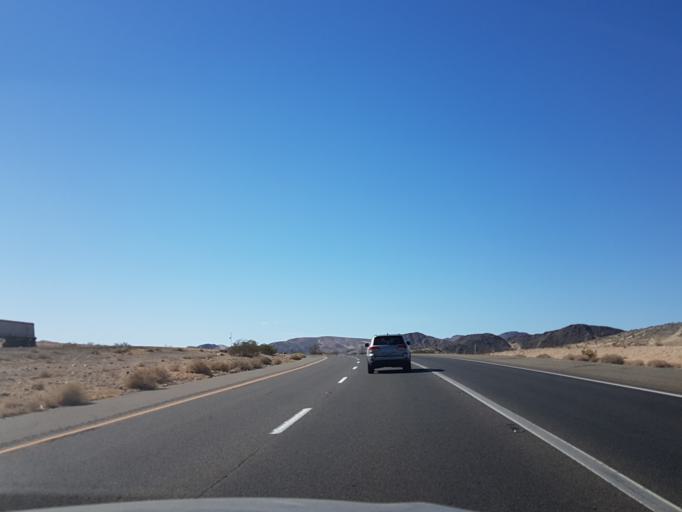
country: US
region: California
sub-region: San Bernardino County
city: Fort Irwin
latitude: 35.0882
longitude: -116.3351
